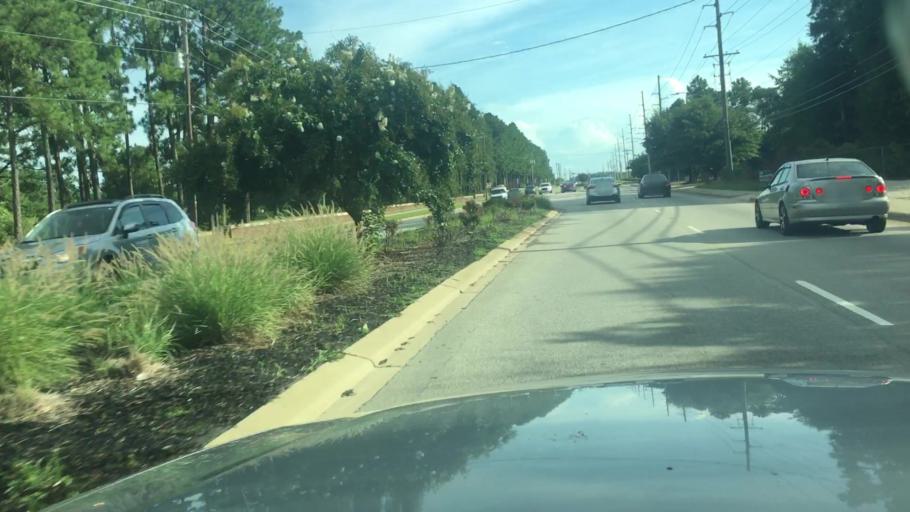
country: US
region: North Carolina
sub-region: Cumberland County
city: Fayetteville
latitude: 35.1364
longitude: -78.8758
